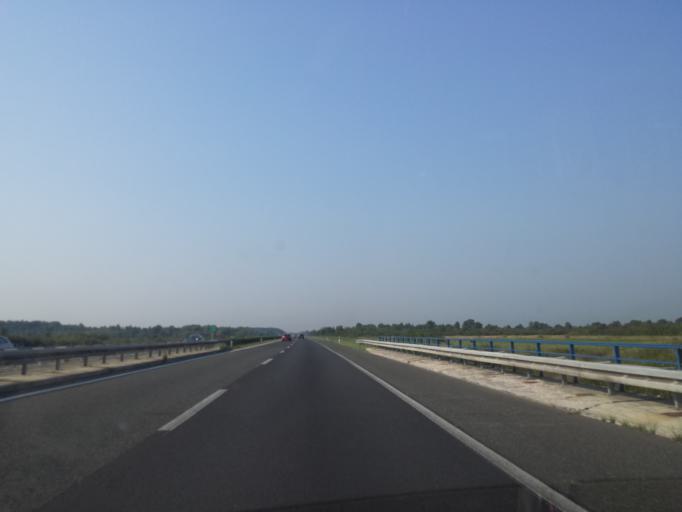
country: HR
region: Zagrebacka
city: Jastrebarsko
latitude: 45.5937
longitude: 15.6306
